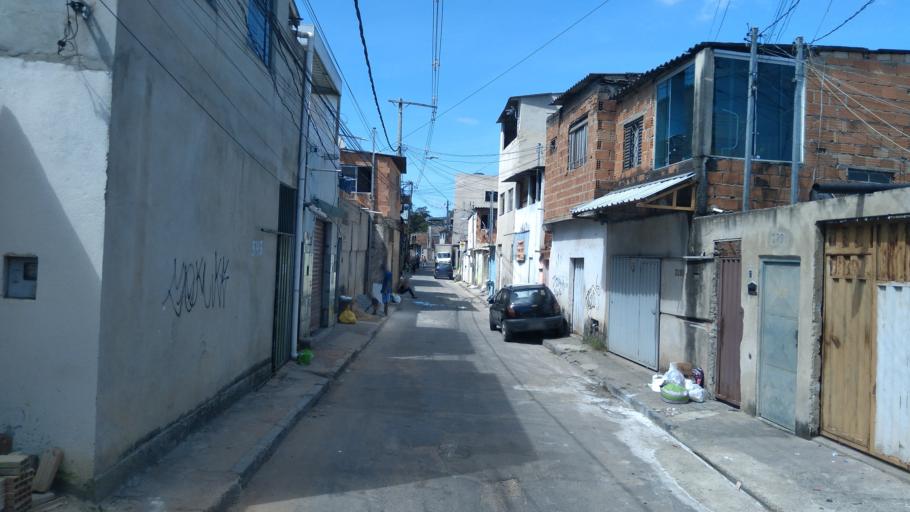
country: BR
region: Minas Gerais
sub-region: Belo Horizonte
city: Belo Horizonte
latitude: -19.8446
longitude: -43.8985
